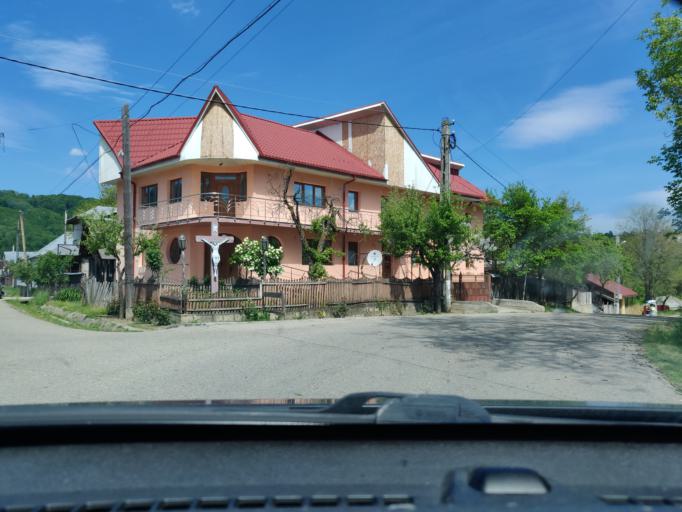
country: RO
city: Vizantea-Manastireasca
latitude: 45.9886
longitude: 26.7749
